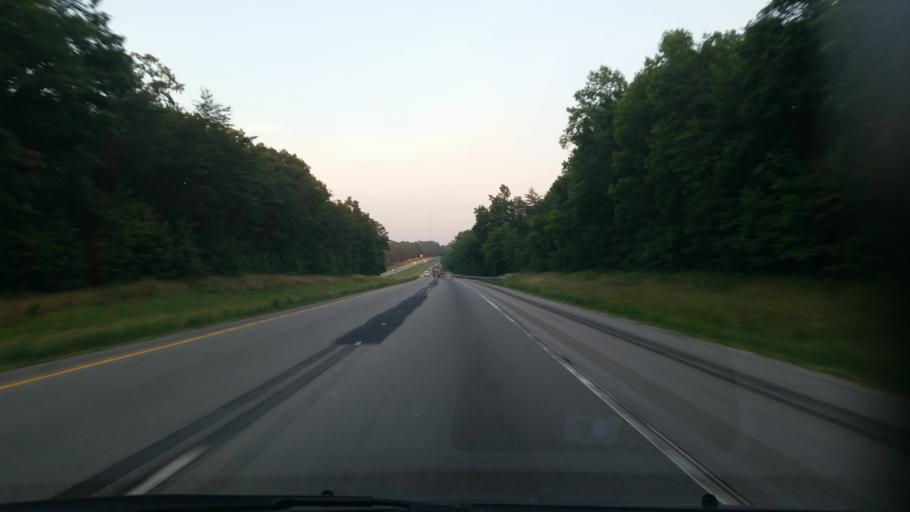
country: US
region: Tennessee
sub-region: Putnam County
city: Monterey
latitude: 36.0756
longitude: -85.2032
